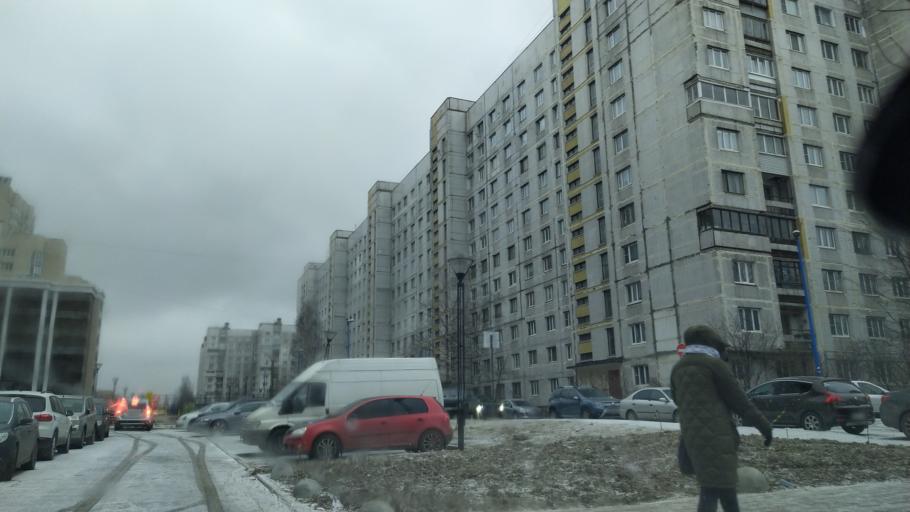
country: RU
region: St.-Petersburg
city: Kupchino
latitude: 59.8401
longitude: 30.3109
